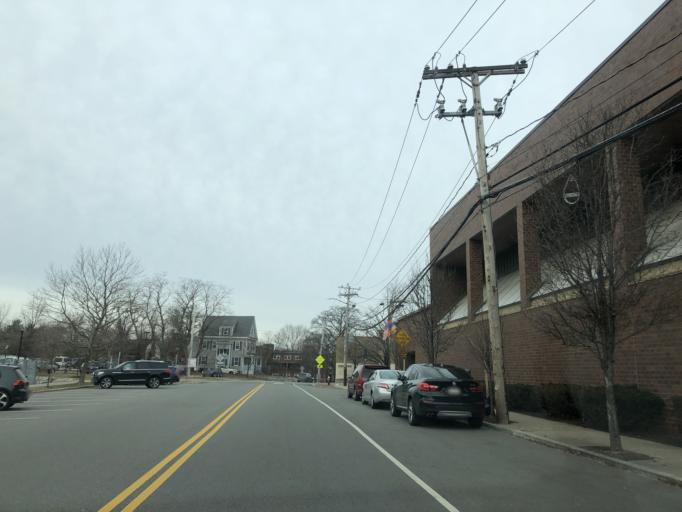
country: US
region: Massachusetts
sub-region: Middlesex County
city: Watertown
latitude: 42.3681
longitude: -71.1581
